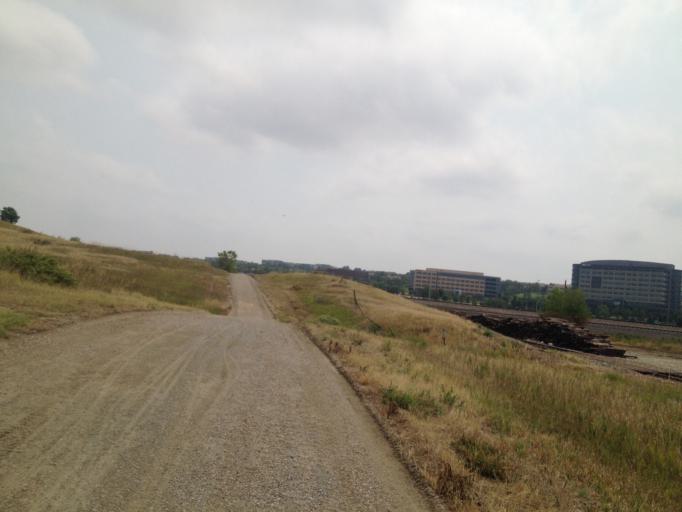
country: US
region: Colorado
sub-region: Broomfield County
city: Broomfield
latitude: 39.9292
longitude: -105.1124
